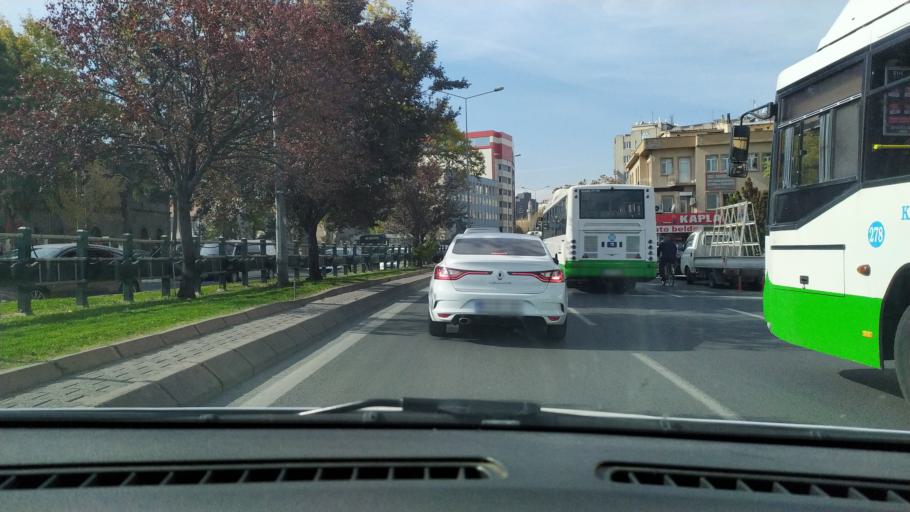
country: TR
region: Kayseri
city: Kayseri
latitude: 38.7171
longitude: 35.4896
